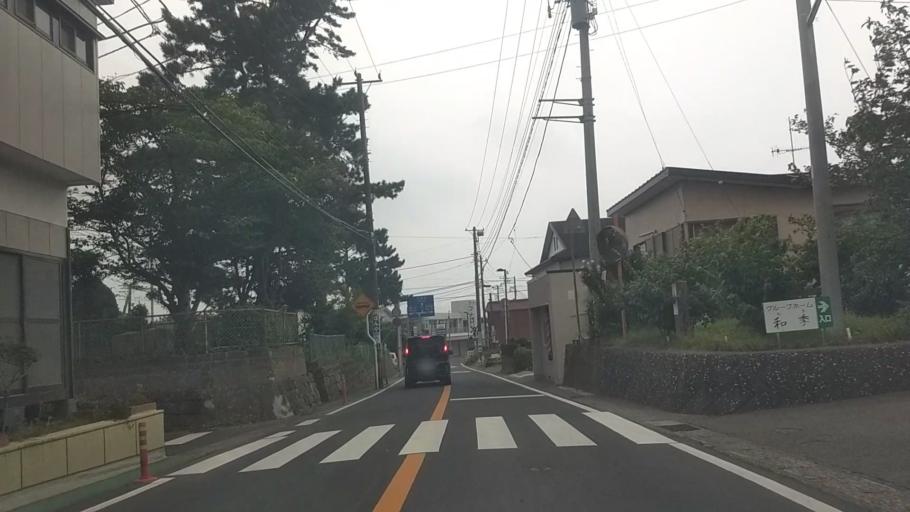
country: JP
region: Chiba
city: Tateyama
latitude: 35.1396
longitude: 139.8408
